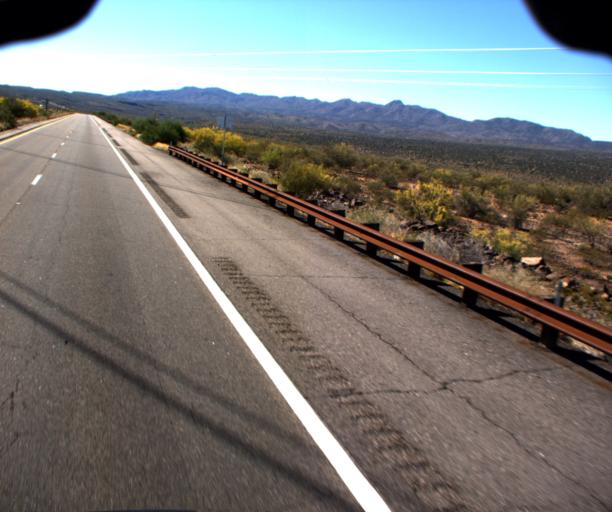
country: US
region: Arizona
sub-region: Yavapai County
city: Bagdad
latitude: 34.5296
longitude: -113.4300
